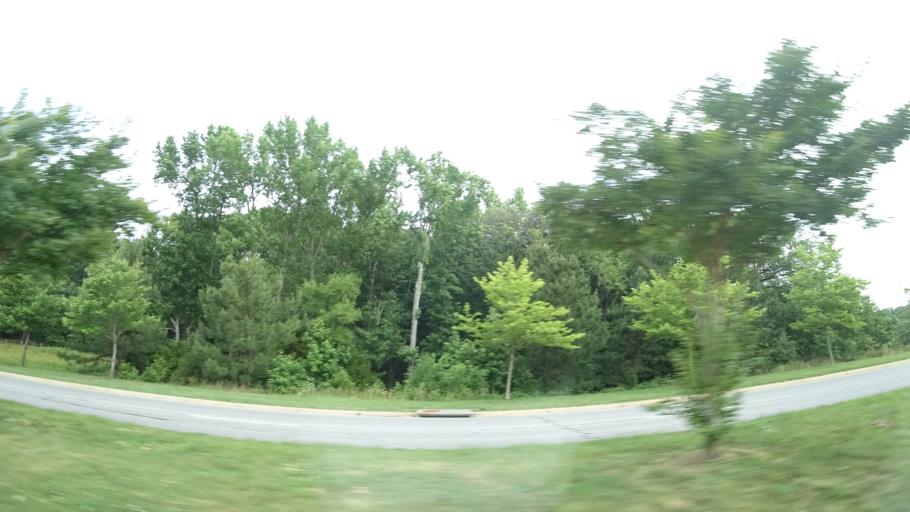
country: US
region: Virginia
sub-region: Spotsylvania County
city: Spotsylvania
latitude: 38.2077
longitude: -77.5837
